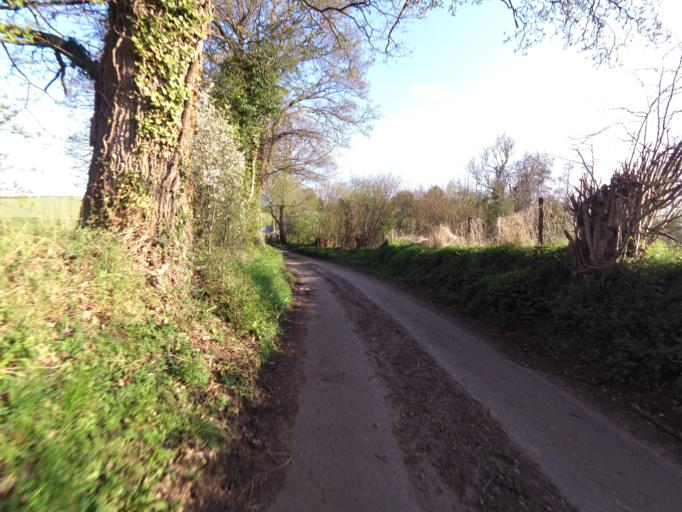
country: GB
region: England
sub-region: Suffolk
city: Bramford
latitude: 52.0415
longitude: 1.0724
